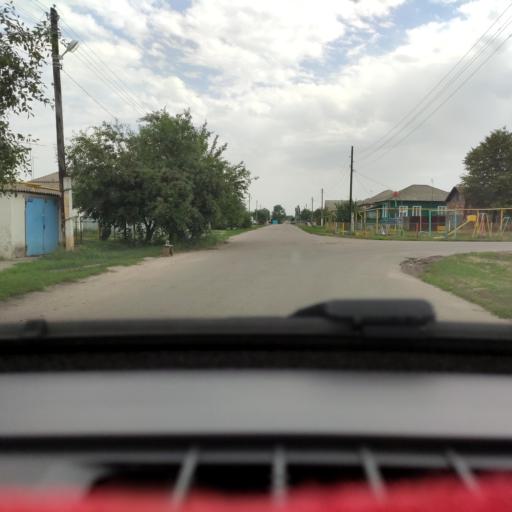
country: RU
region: Voronezj
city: Davydovka
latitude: 51.1955
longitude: 39.4913
